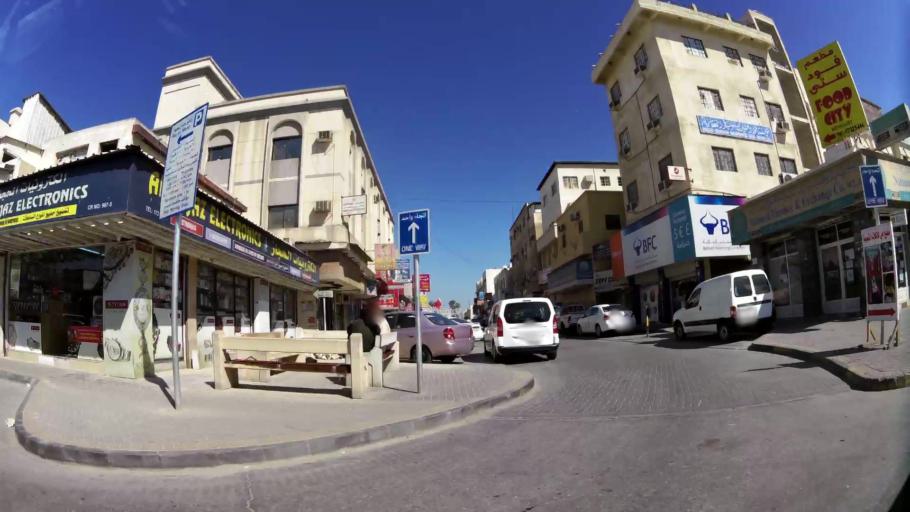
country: BH
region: Muharraq
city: Al Muharraq
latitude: 26.2507
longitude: 50.6086
